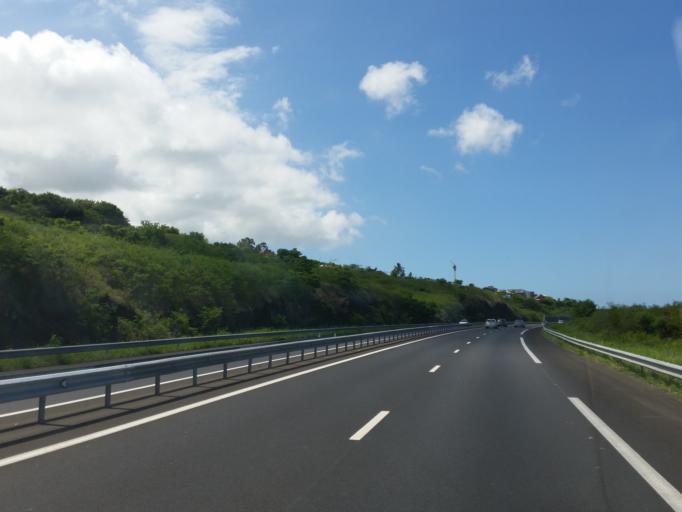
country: RE
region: Reunion
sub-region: Reunion
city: Saint-Leu
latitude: -21.1860
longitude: 55.2969
